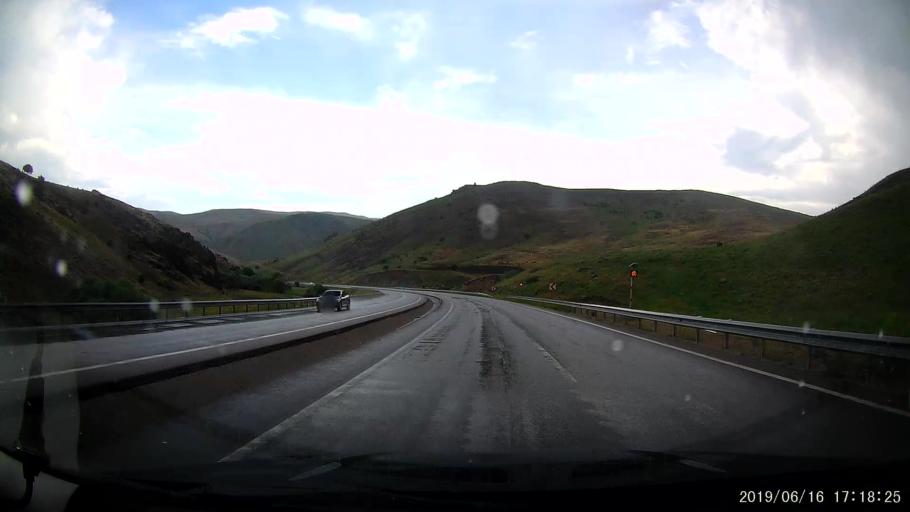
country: TR
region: Erzincan
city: Tercan
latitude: 39.8147
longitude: 40.5288
